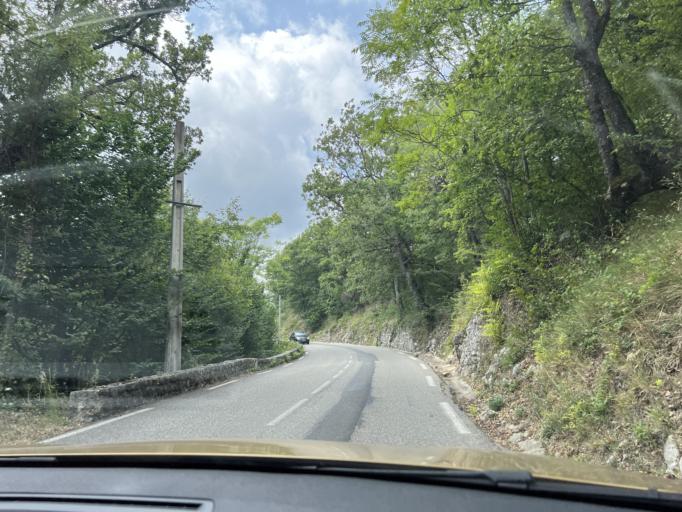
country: FR
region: Provence-Alpes-Cote d'Azur
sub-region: Departement des Alpes-Maritimes
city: Tourrettes-sur-Loup
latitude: 43.7948
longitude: 6.9622
